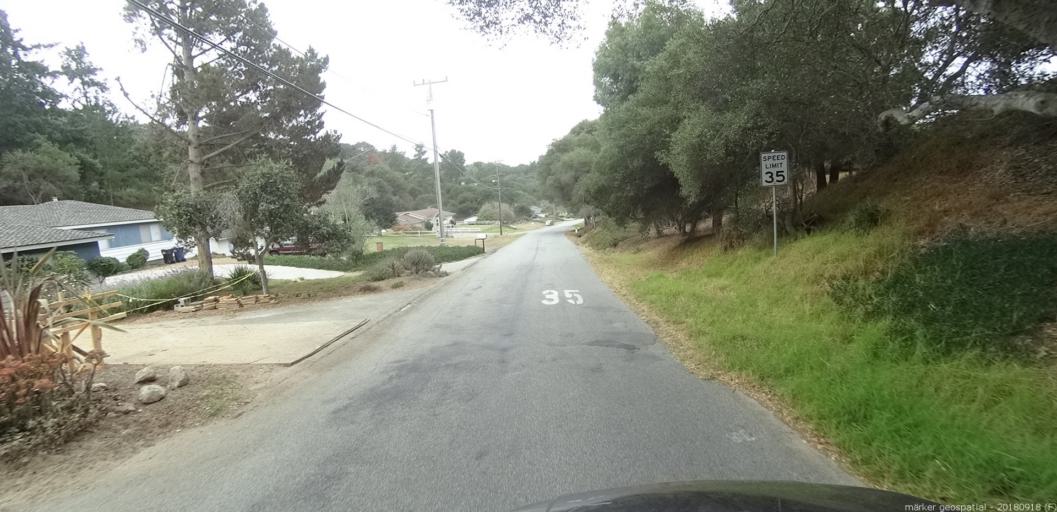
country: US
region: California
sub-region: Monterey County
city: Prunedale
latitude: 36.7912
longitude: -121.6512
